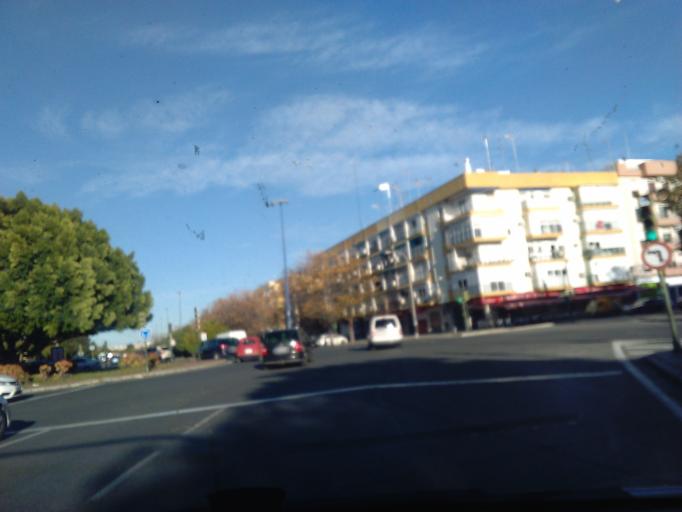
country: ES
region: Andalusia
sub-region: Provincia de Sevilla
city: Sevilla
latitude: 37.3731
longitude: -5.9647
